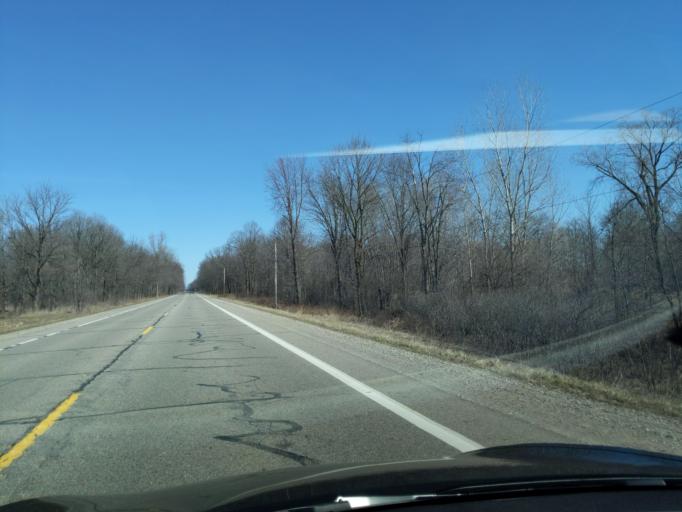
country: US
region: Michigan
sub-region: Ionia County
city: Lake Odessa
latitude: 42.7308
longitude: -85.0895
